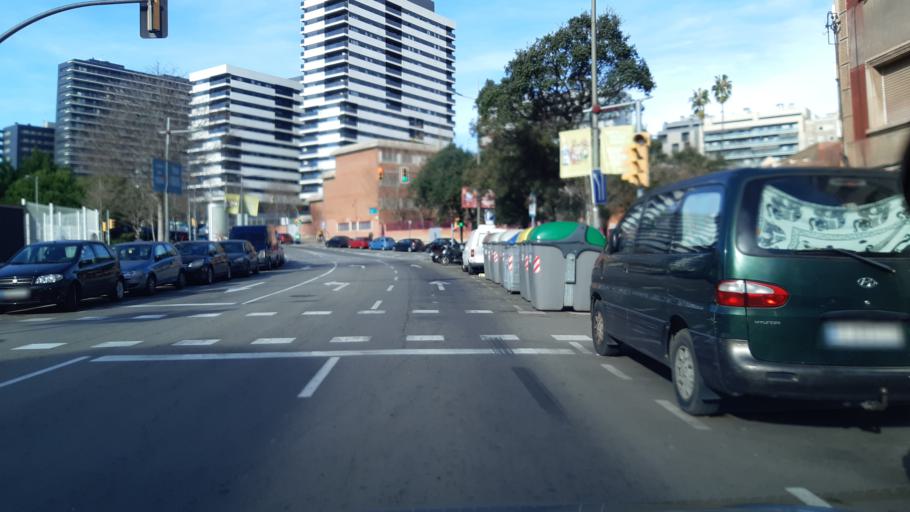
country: ES
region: Catalonia
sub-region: Provincia de Barcelona
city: L'Hospitalet de Llobregat
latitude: 41.3740
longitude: 2.1119
